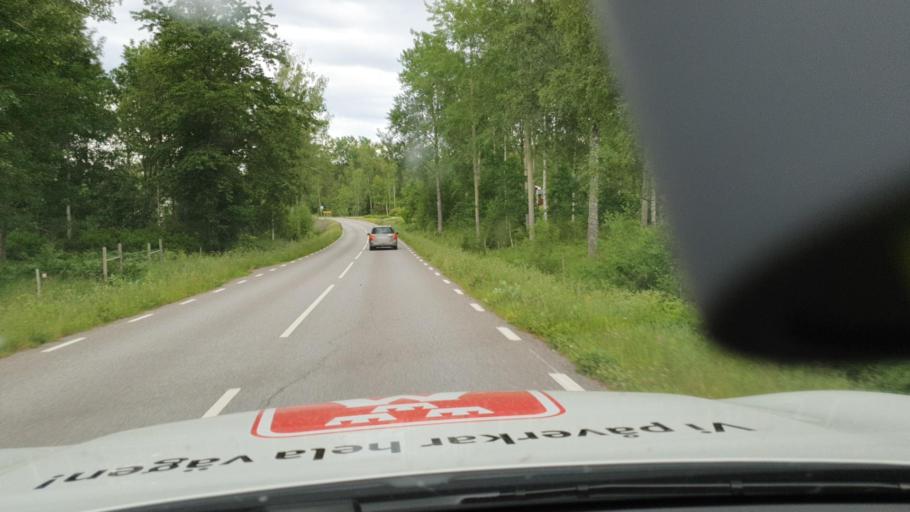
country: SE
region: Vaestra Goetaland
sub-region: Karlsborgs Kommun
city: Karlsborg
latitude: 58.7476
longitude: 14.5073
